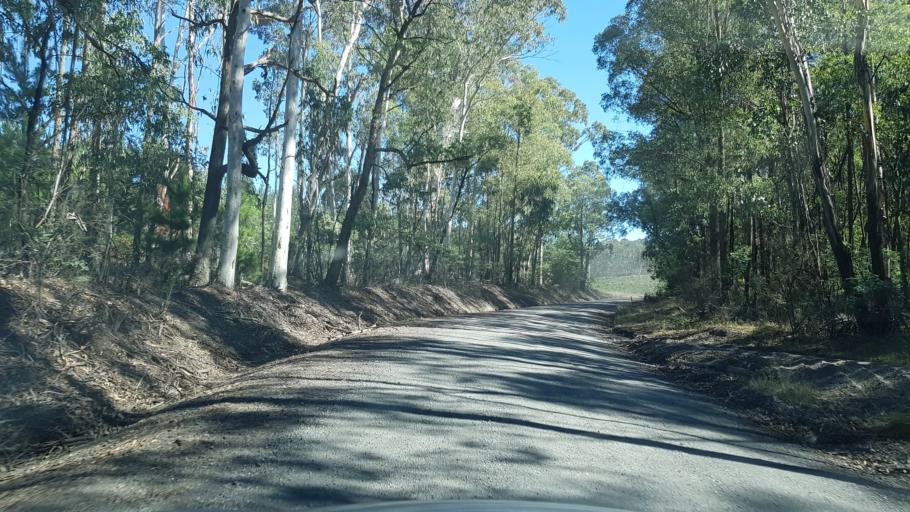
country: AU
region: Victoria
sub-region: Mansfield
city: Mansfield
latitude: -36.8505
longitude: 146.5090
